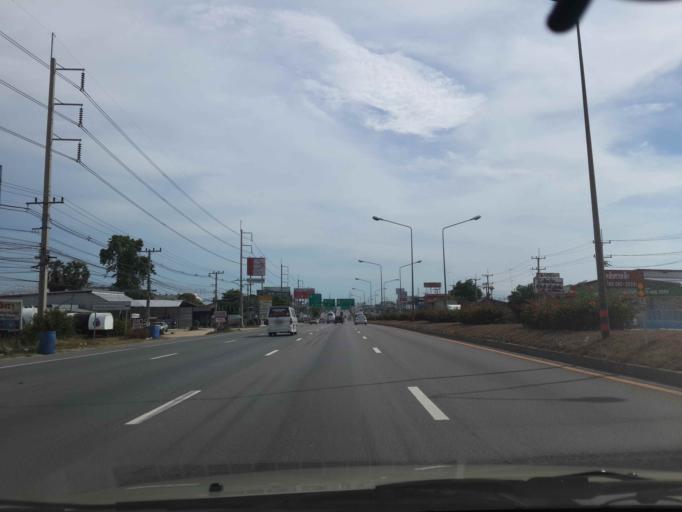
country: TH
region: Chon Buri
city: Chon Buri
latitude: 13.3585
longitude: 101.0118
